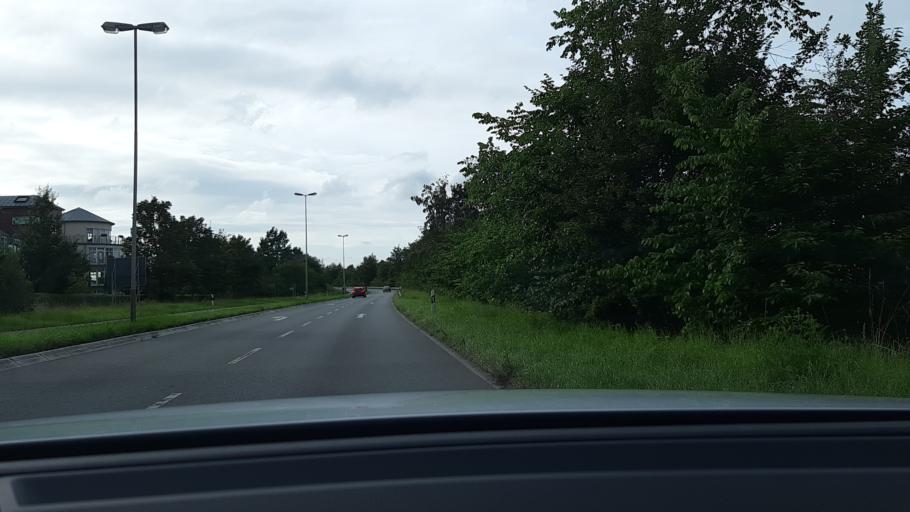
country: DE
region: Schleswig-Holstein
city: Stockelsdorf
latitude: 53.8895
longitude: 10.6394
